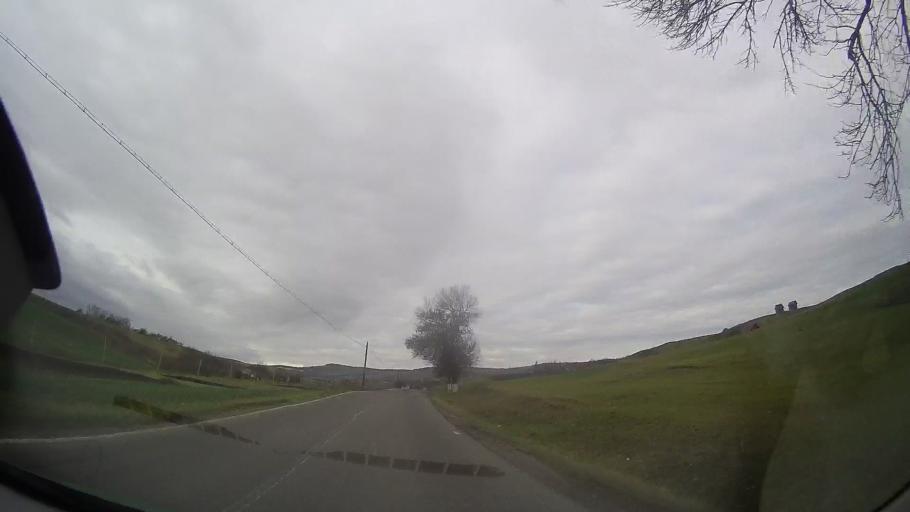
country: RO
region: Bistrita-Nasaud
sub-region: Comuna Urmenis
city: Urmenis
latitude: 46.7621
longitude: 24.3803
